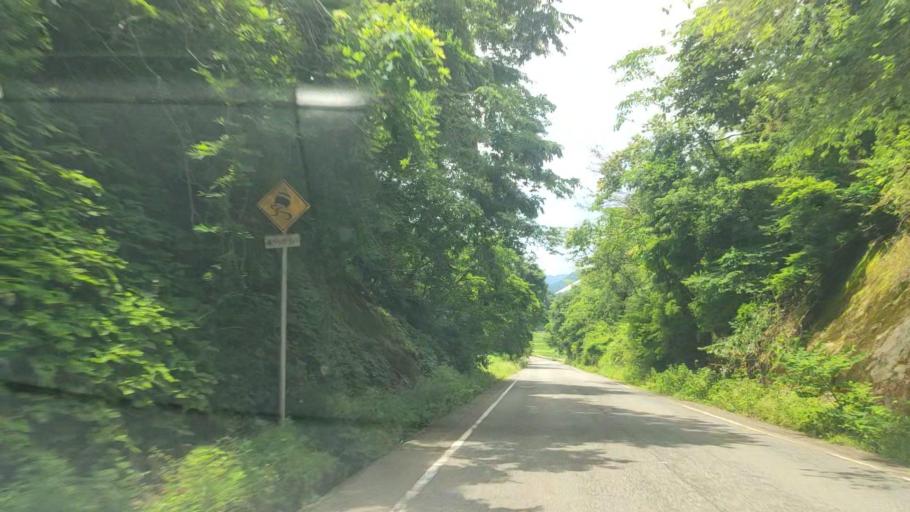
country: JP
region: Hyogo
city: Toyooka
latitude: 35.5083
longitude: 134.6852
